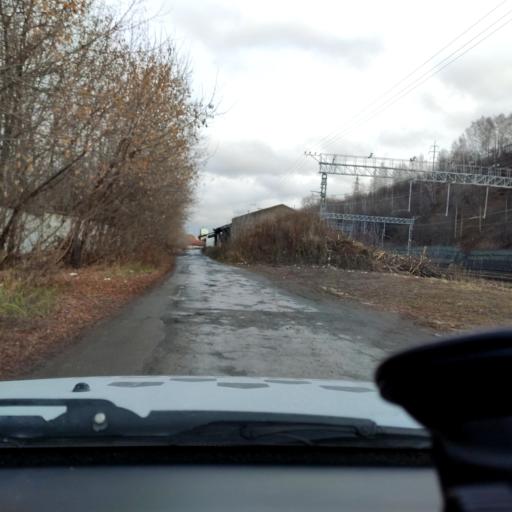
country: RU
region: Perm
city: Perm
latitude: 58.0247
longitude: 56.2692
